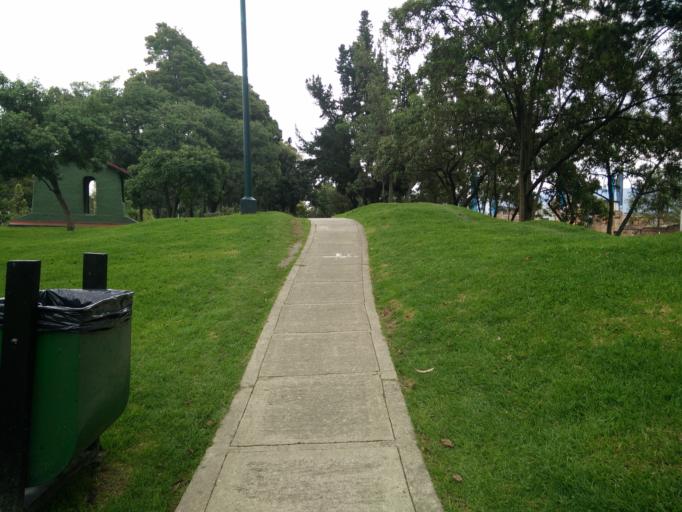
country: CO
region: Bogota D.C.
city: Bogota
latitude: 4.6548
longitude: -74.0802
